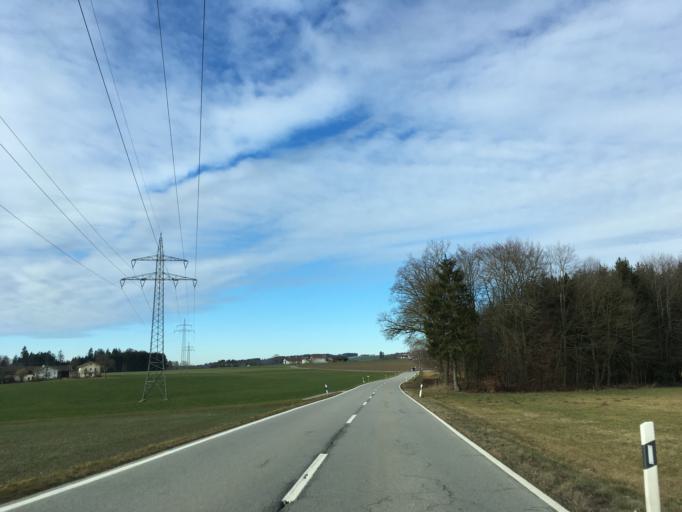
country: DE
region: Bavaria
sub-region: Upper Bavaria
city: Gars
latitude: 48.1669
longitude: 12.2680
